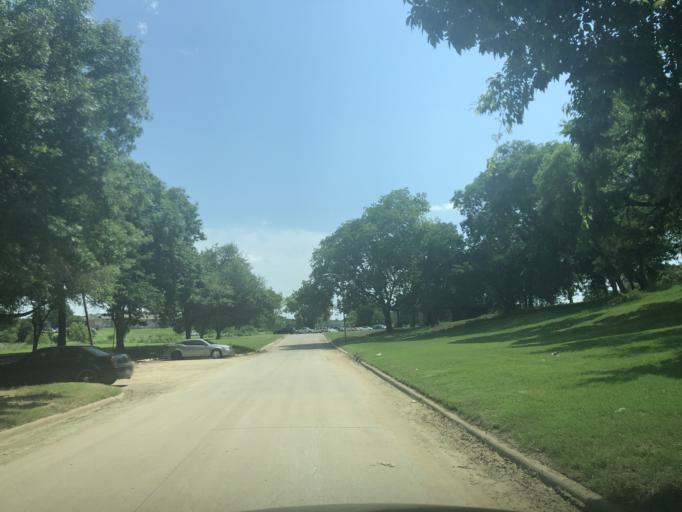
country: US
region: Texas
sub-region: Dallas County
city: Grand Prairie
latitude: 32.7242
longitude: -97.0144
